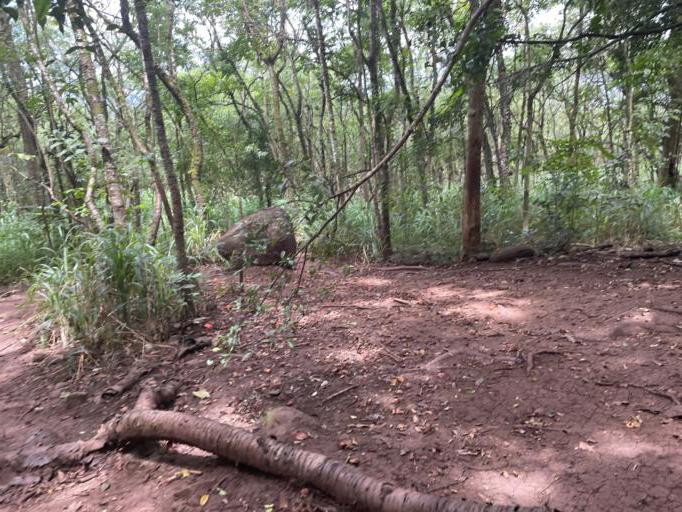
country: US
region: Hawaii
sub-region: Honolulu County
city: Pupukea
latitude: 21.6633
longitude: -158.0472
